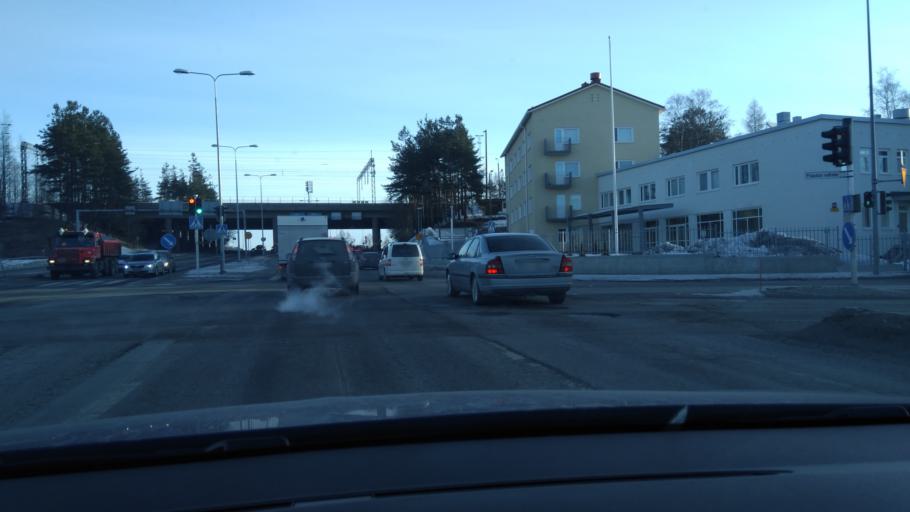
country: FI
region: Pirkanmaa
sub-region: Tampere
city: Pirkkala
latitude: 61.5081
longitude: 23.6878
